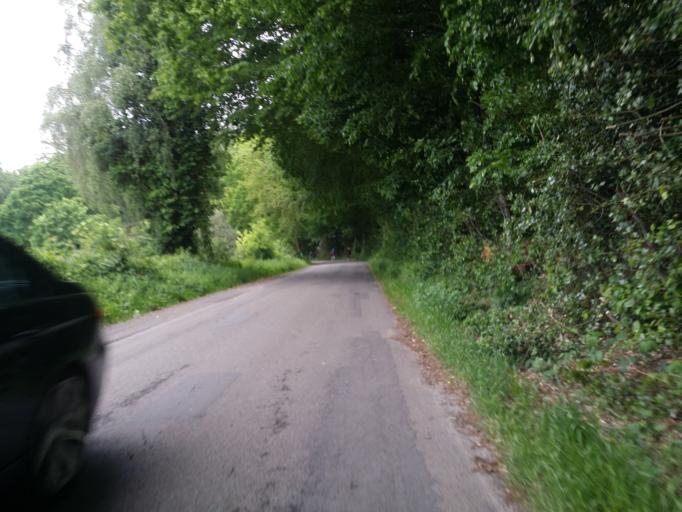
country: DE
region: Lower Saxony
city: Rastede
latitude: 53.2330
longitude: 8.2485
